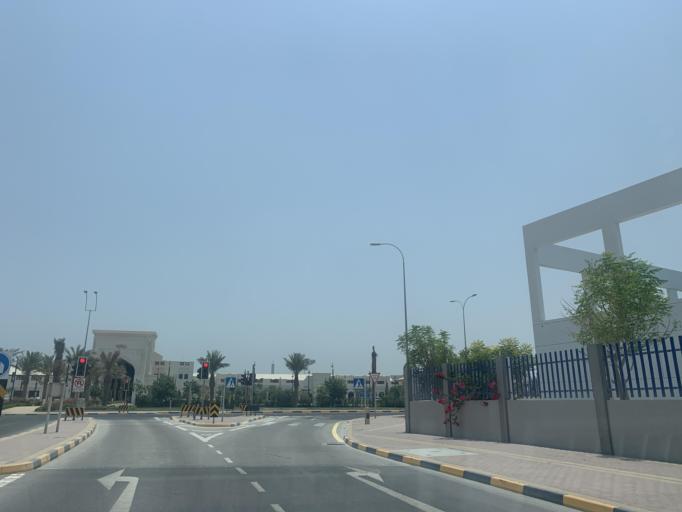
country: BH
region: Muharraq
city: Al Muharraq
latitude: 26.3058
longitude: 50.6356
